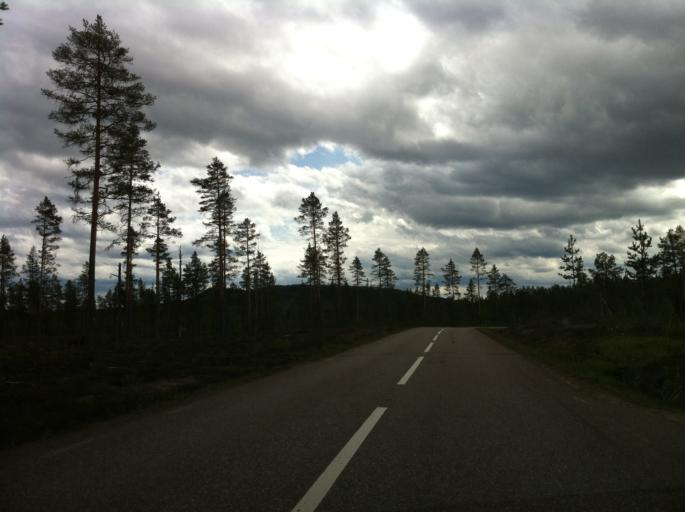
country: NO
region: Hedmark
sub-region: Trysil
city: Innbygda
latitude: 61.4280
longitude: 13.0886
